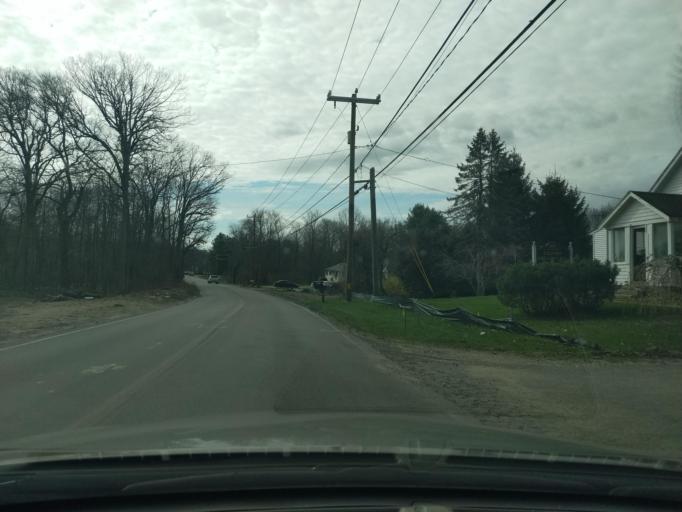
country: US
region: Connecticut
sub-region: Fairfield County
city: Newtown
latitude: 41.3427
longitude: -73.2486
